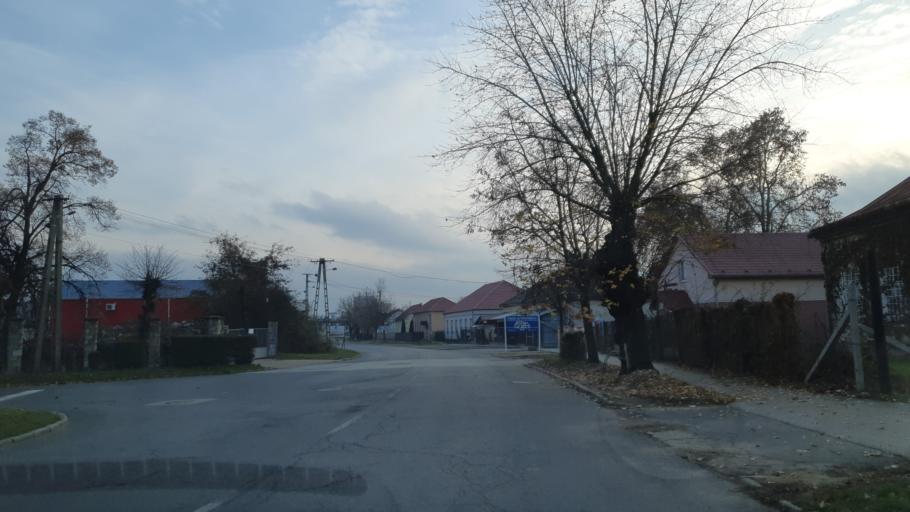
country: HU
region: Szabolcs-Szatmar-Bereg
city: Kisvarda
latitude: 48.2124
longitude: 22.0802
